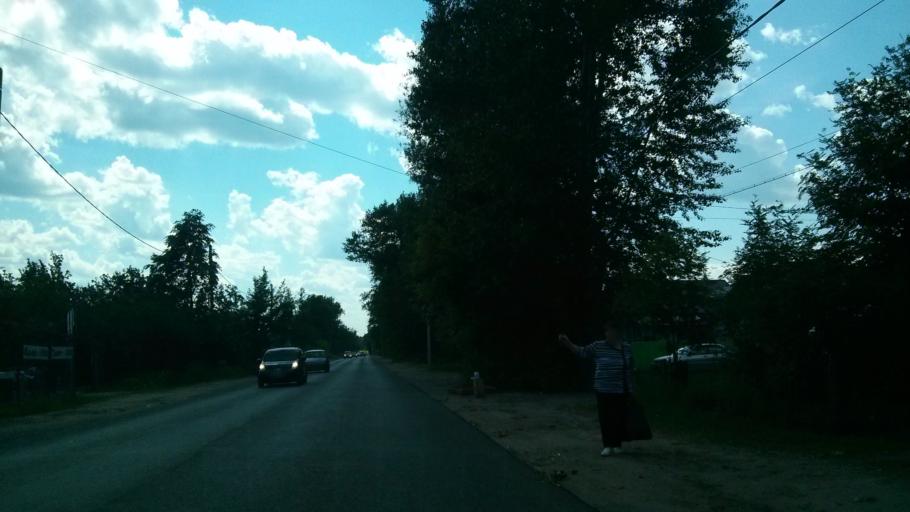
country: RU
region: Vladimir
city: Murom
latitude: 55.5329
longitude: 41.9678
